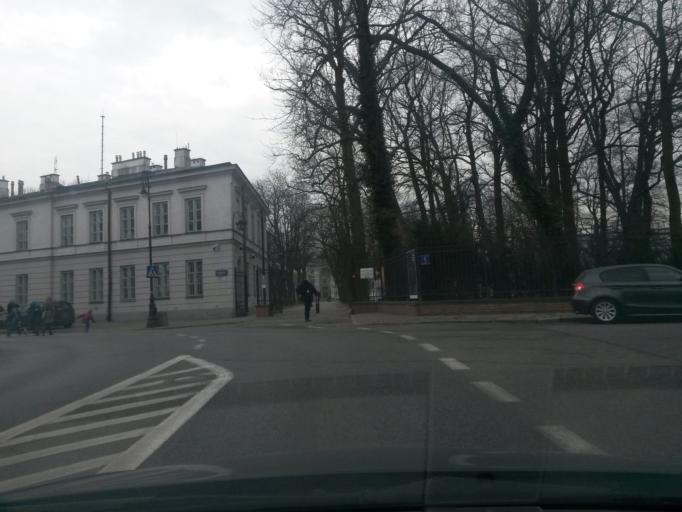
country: PL
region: Masovian Voivodeship
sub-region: Warszawa
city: Mokotow
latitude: 52.2172
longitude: 21.0376
